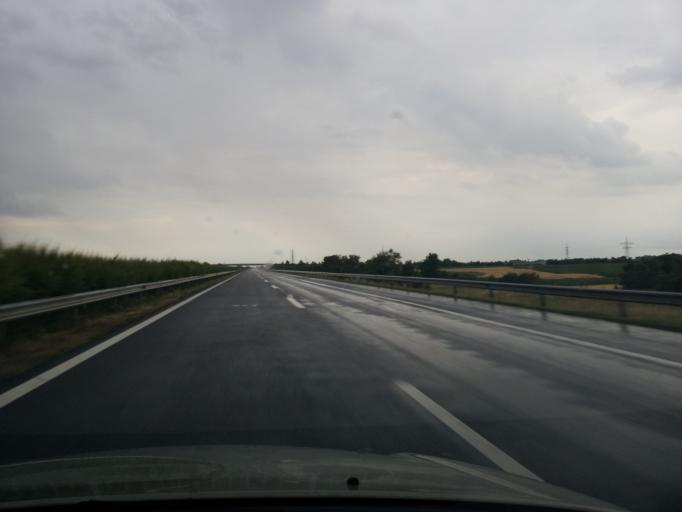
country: HU
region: Borsod-Abauj-Zemplen
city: Onod
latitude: 48.0046
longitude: 20.8840
